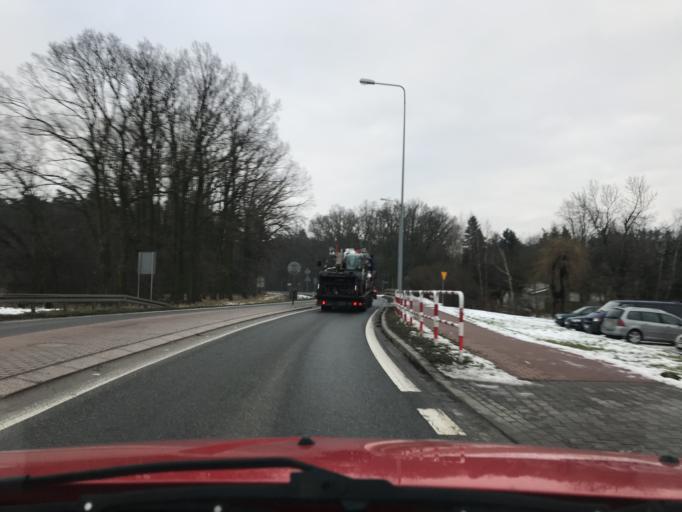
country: PL
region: Greater Poland Voivodeship
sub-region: Powiat pleszewski
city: Goluchow
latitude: 51.8476
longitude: 17.9379
